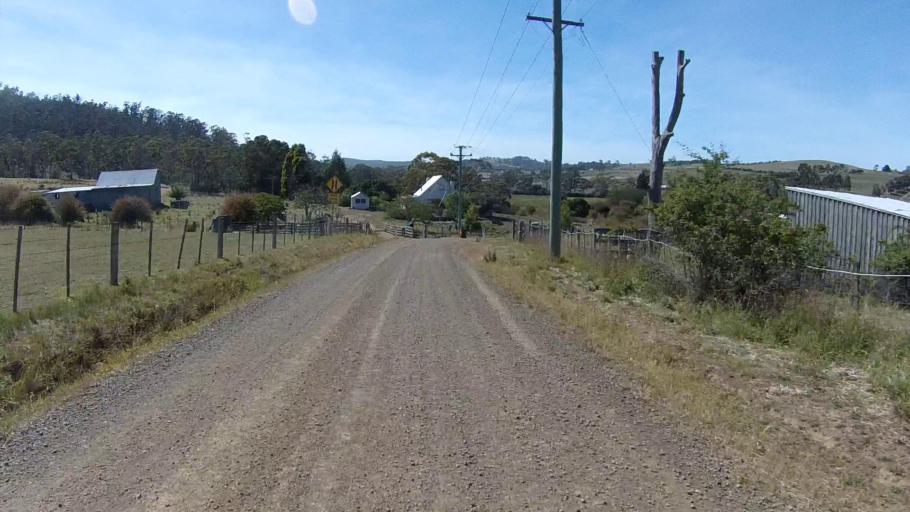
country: AU
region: Tasmania
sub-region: Sorell
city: Sorell
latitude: -42.7499
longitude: 147.6240
